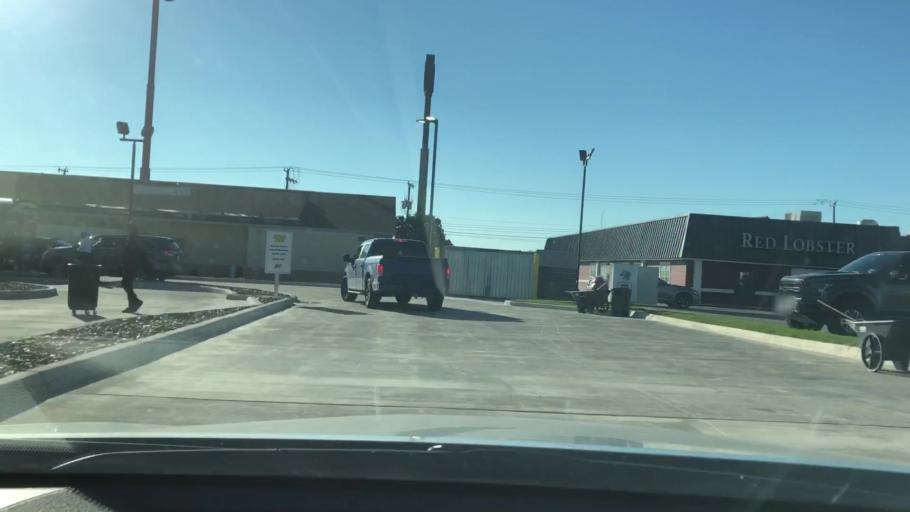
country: US
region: Texas
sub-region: Bexar County
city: Windcrest
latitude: 29.5126
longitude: -98.3954
